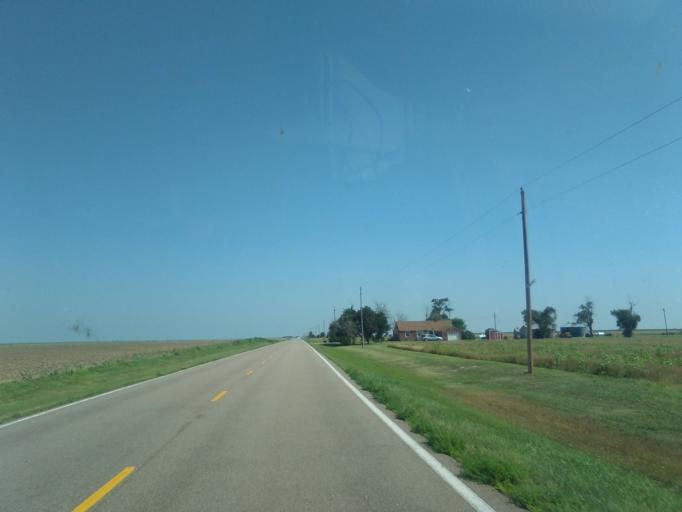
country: US
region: Kansas
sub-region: Cheyenne County
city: Saint Francis
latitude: 39.7906
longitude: -101.5419
